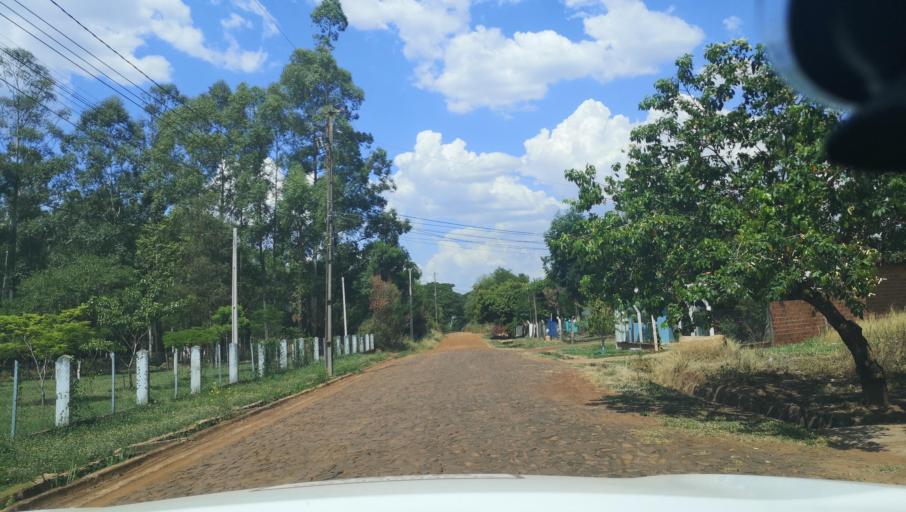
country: PY
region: Itapua
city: Carmen del Parana
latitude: -27.1713
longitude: -56.2285
